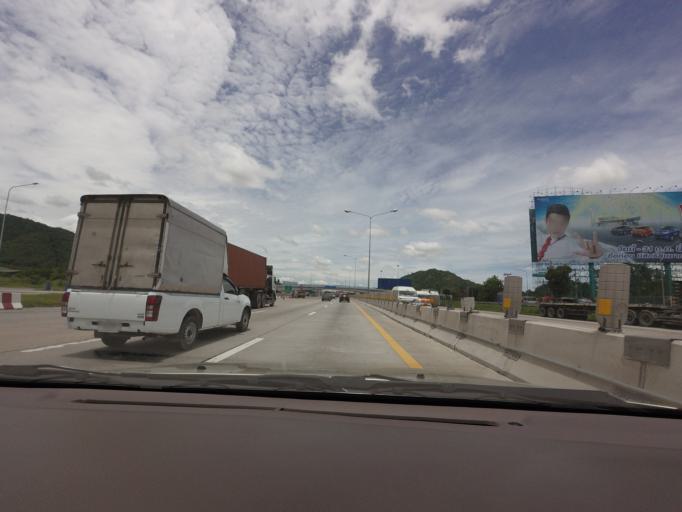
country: TH
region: Chon Buri
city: Chon Buri
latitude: 13.2885
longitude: 100.9915
